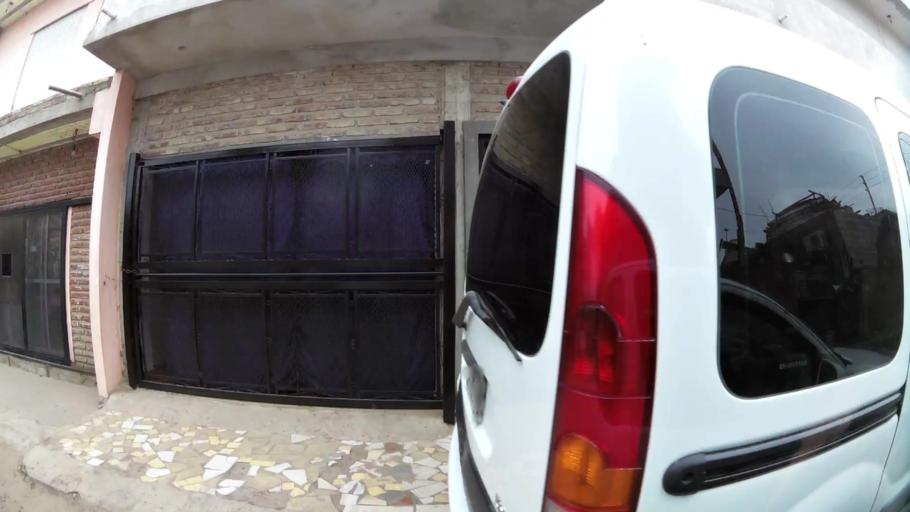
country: AR
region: Buenos Aires
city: San Justo
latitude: -34.7009
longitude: -58.5509
